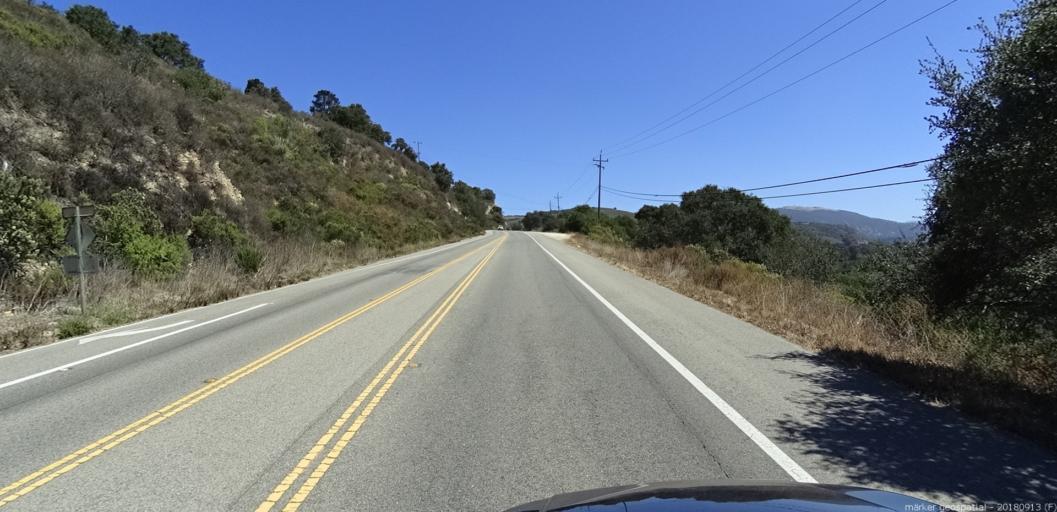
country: US
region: California
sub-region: Monterey County
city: Carmel Valley Village
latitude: 36.5229
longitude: -121.8026
